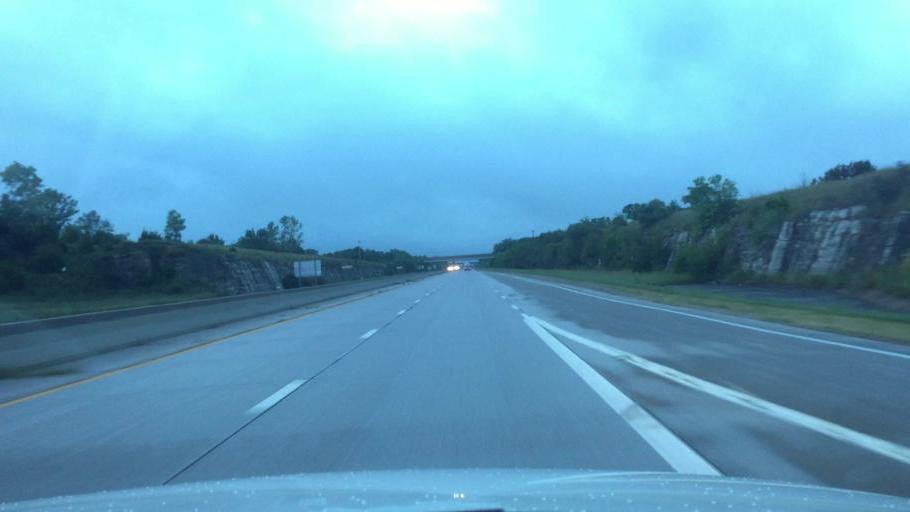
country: US
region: Kansas
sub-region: Neosho County
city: Chanute
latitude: 37.6865
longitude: -95.4796
